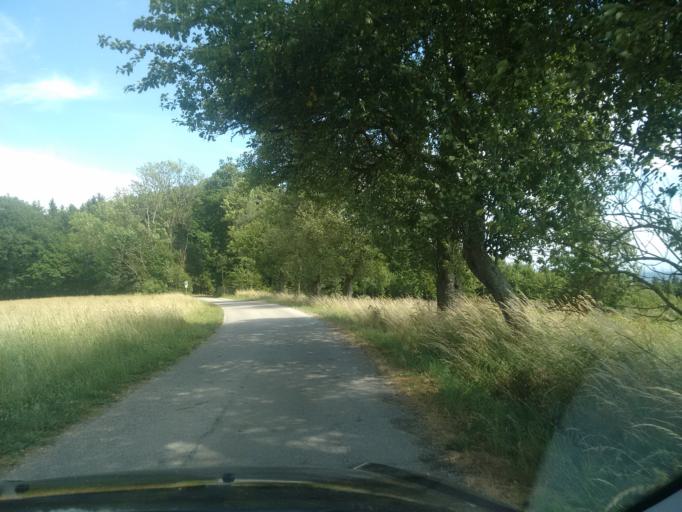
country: AT
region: Upper Austria
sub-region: Wels-Land
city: Gunskirchen
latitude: 48.1734
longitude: 13.9285
